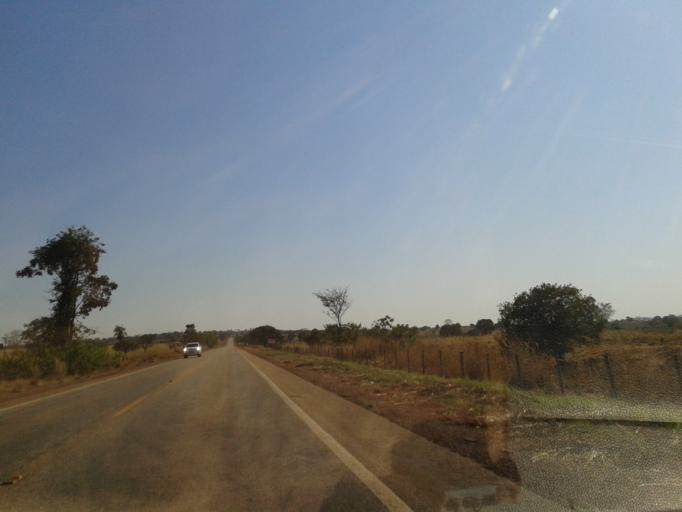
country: BR
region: Goias
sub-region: Mozarlandia
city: Mozarlandia
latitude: -14.7132
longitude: -50.5461
